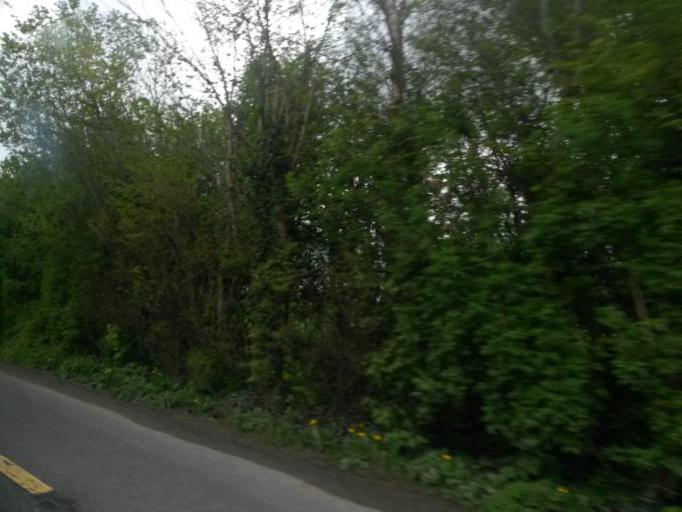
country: IE
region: Leinster
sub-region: Loch Garman
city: Enniscorthy
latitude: 52.4347
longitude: -6.5352
